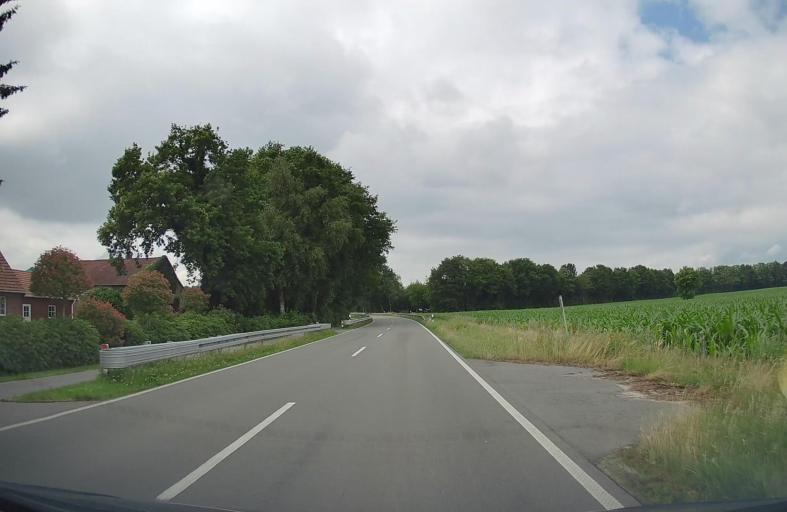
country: DE
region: Lower Saxony
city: Friesoythe
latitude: 53.0544
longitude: 7.8100
